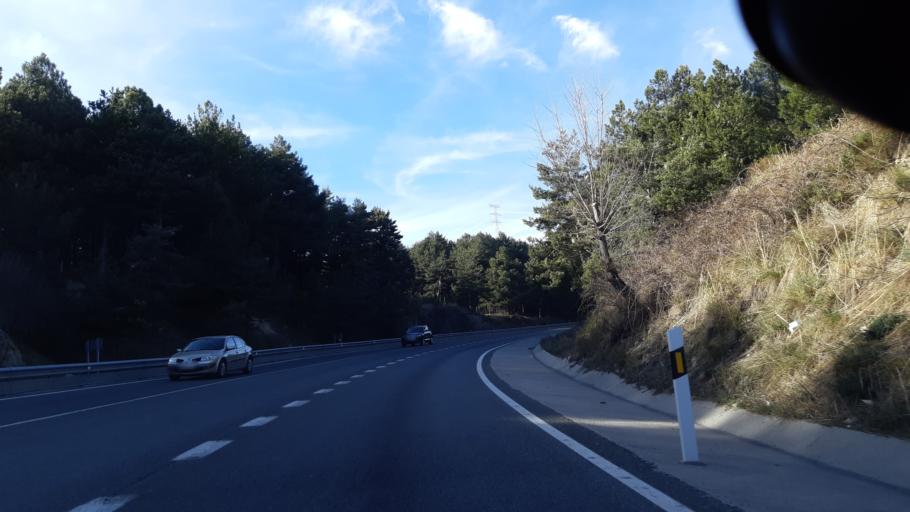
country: ES
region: Madrid
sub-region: Provincia de Madrid
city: Guadarrama
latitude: 40.7071
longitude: -4.1325
